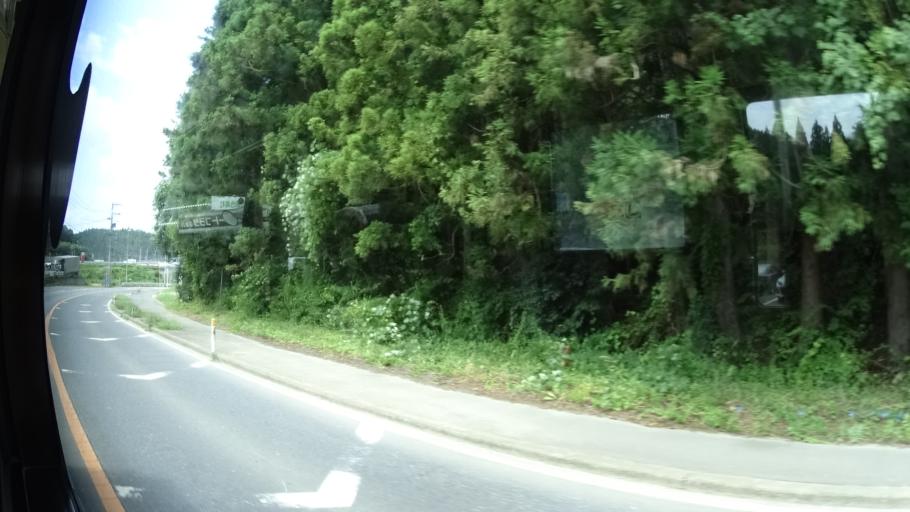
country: JP
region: Miyagi
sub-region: Oshika Gun
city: Onagawa Cho
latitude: 38.6883
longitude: 141.4583
